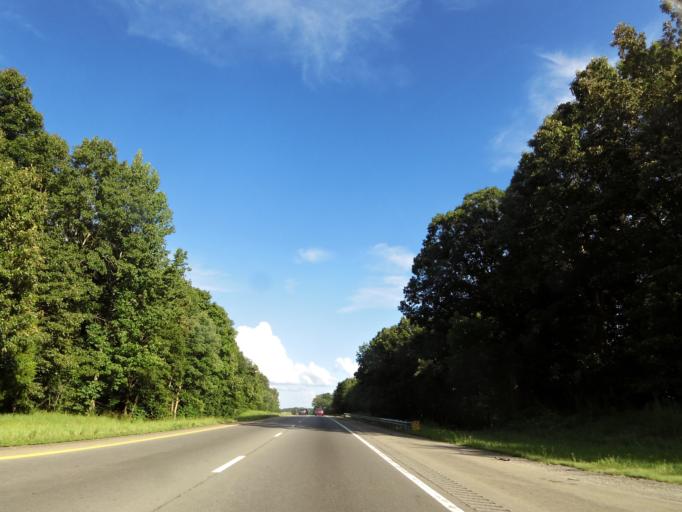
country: US
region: Tennessee
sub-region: Cheatham County
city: Pleasant View
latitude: 36.4085
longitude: -87.0371
